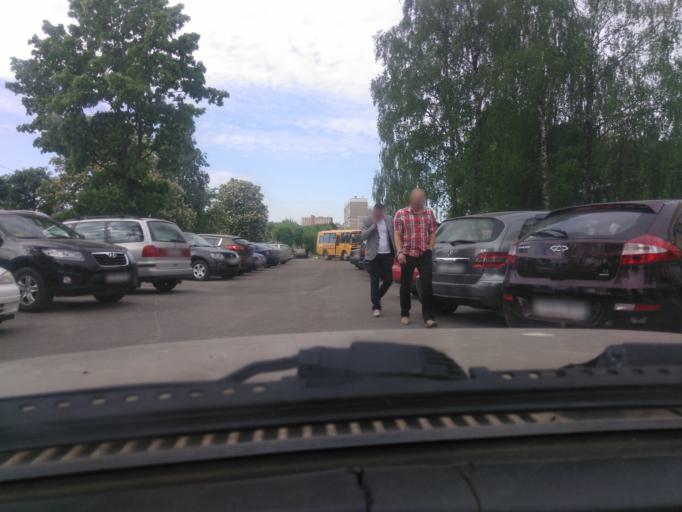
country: BY
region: Mogilev
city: Mahilyow
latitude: 53.9030
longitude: 30.3009
